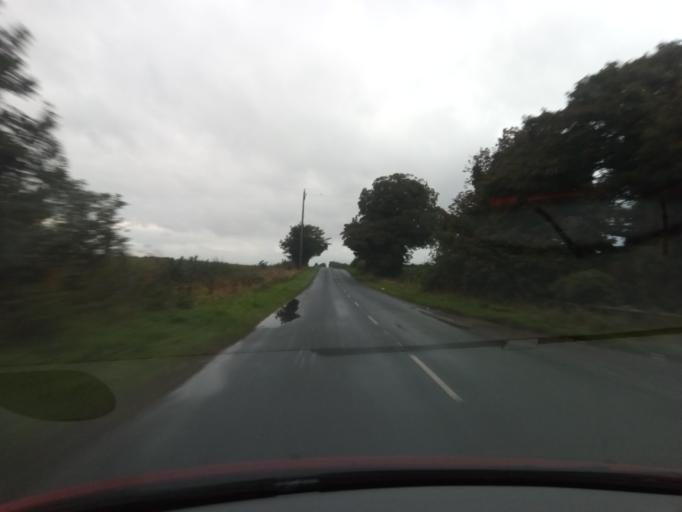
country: GB
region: England
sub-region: Darlington
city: High Coniscliffe
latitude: 54.4891
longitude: -1.6703
